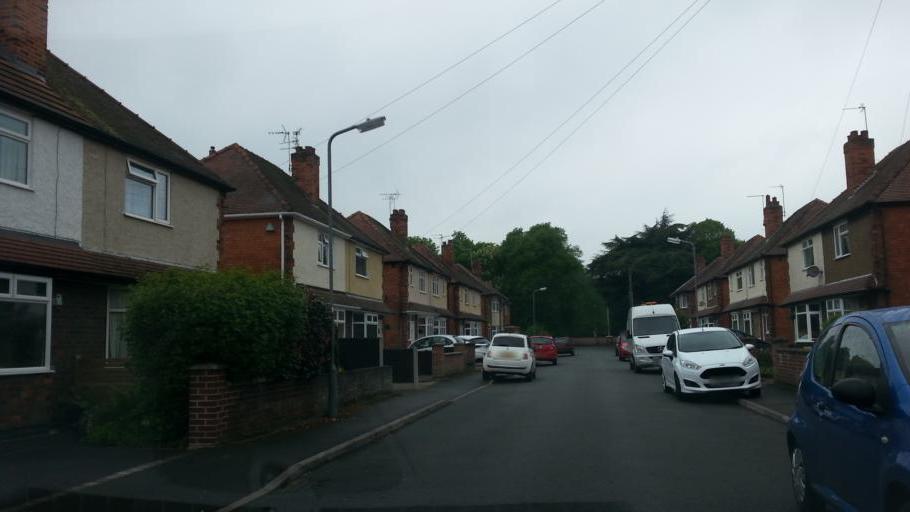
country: GB
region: England
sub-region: Nottinghamshire
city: Newark on Trent
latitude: 53.0649
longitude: -0.7971
